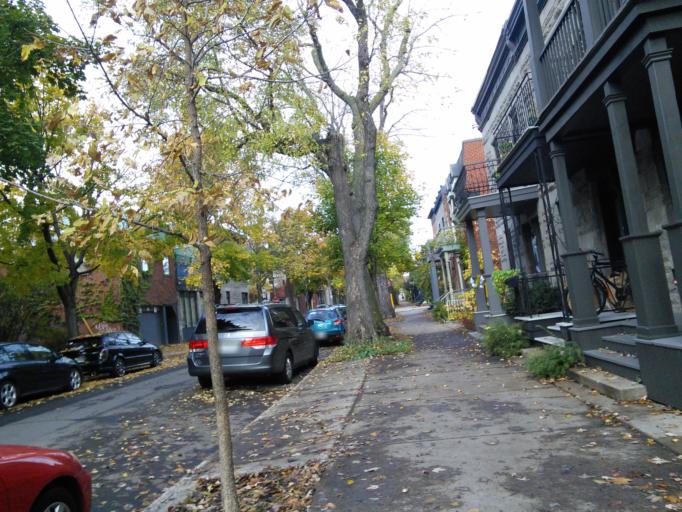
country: CA
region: Quebec
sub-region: Montreal
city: Montreal
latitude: 45.5269
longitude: -73.5817
